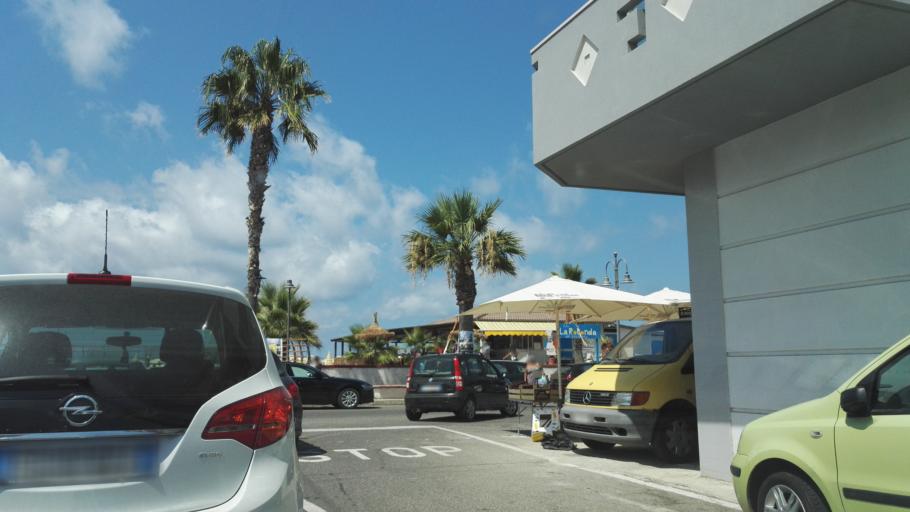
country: IT
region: Calabria
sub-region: Provincia di Vibo-Valentia
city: Nicotera
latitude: 38.5461
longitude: 15.9321
